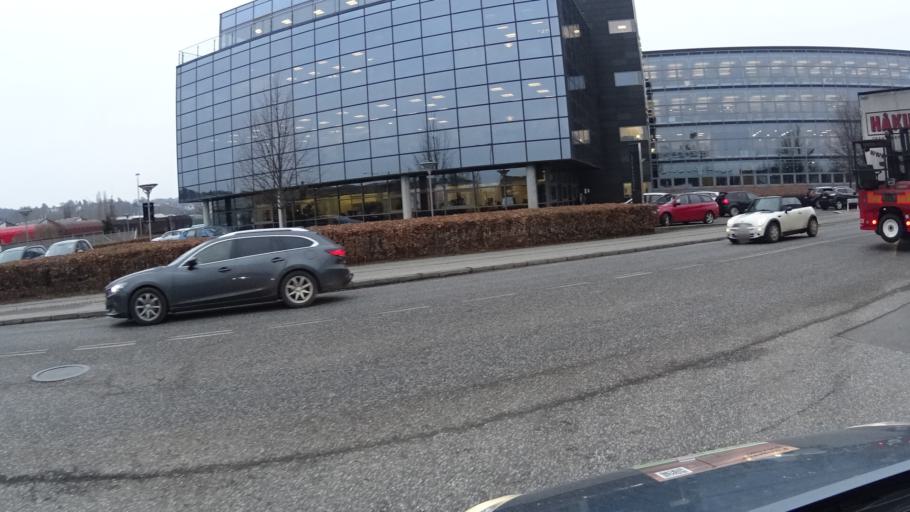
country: DK
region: South Denmark
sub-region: Vejle Kommune
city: Vejle
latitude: 55.7060
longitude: 9.5425
